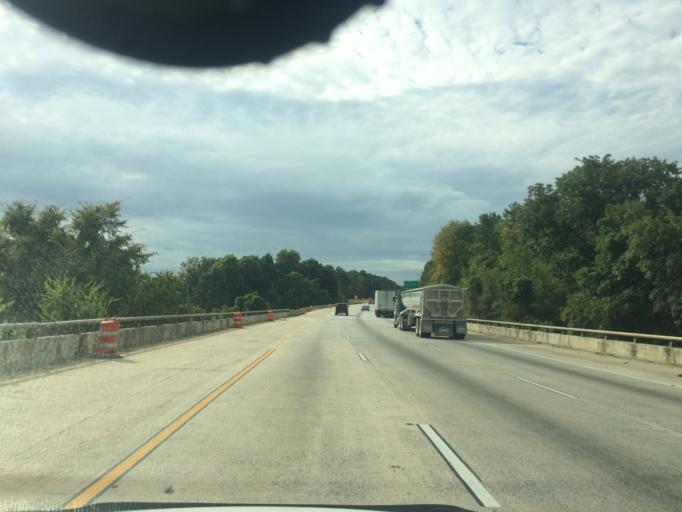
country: US
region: Georgia
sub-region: Cobb County
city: Kennesaw
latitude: 34.0228
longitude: -84.5720
